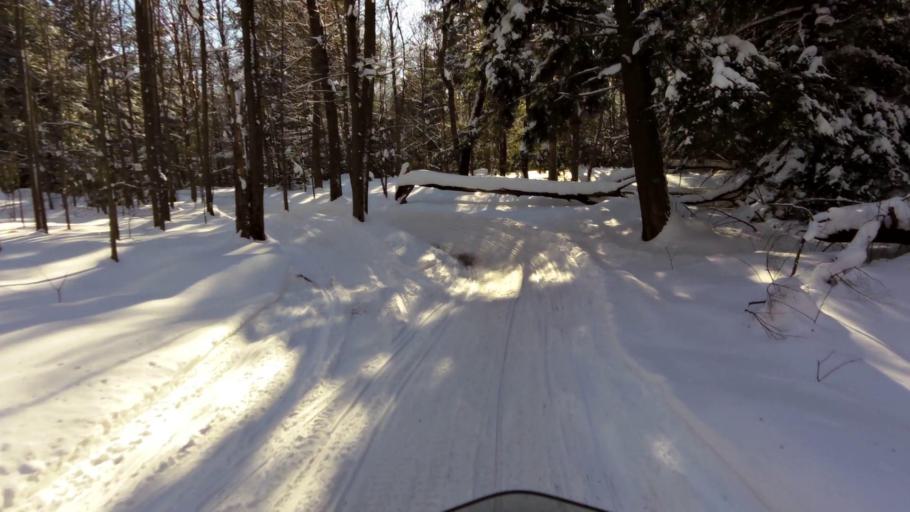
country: US
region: New York
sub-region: Chautauqua County
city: Mayville
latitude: 42.1523
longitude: -79.5748
